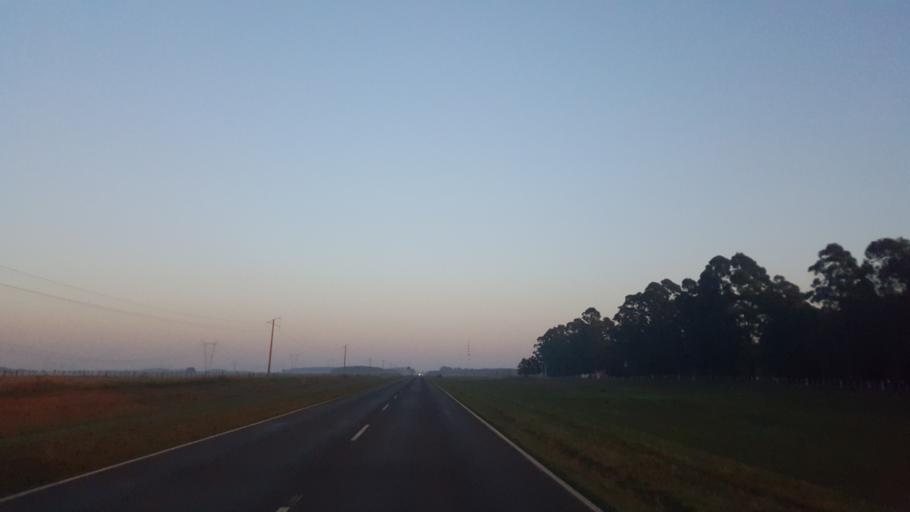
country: AR
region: Corrientes
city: Ituzaingo
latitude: -27.5913
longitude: -56.4775
